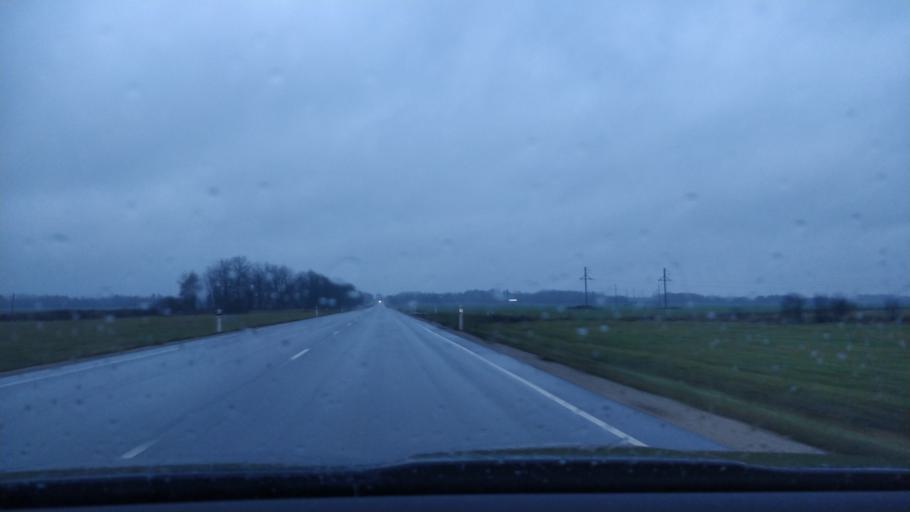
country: EE
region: Laeaene
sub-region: Lihula vald
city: Lihula
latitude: 58.7311
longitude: 23.9767
